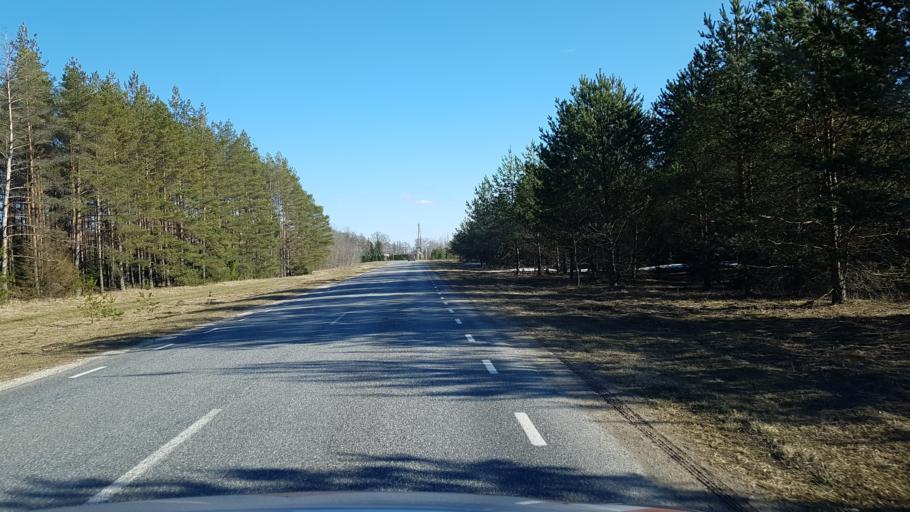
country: EE
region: Laeaene-Virumaa
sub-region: Haljala vald
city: Haljala
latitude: 59.4668
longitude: 26.1813
